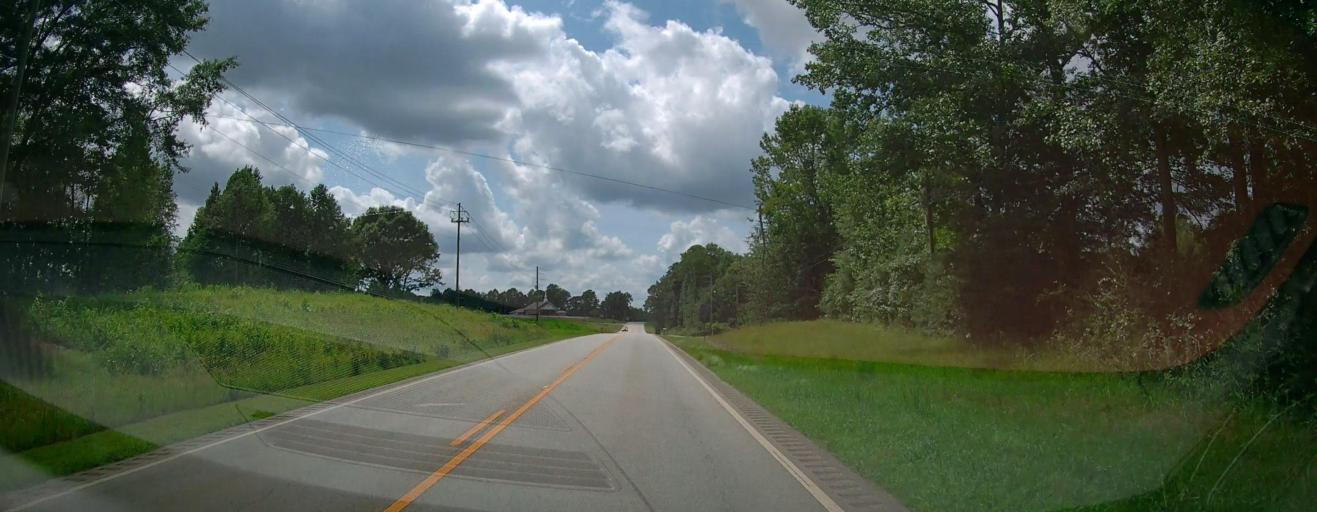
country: US
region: Georgia
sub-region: Carroll County
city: Bowdon
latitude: 33.5394
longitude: -85.3849
